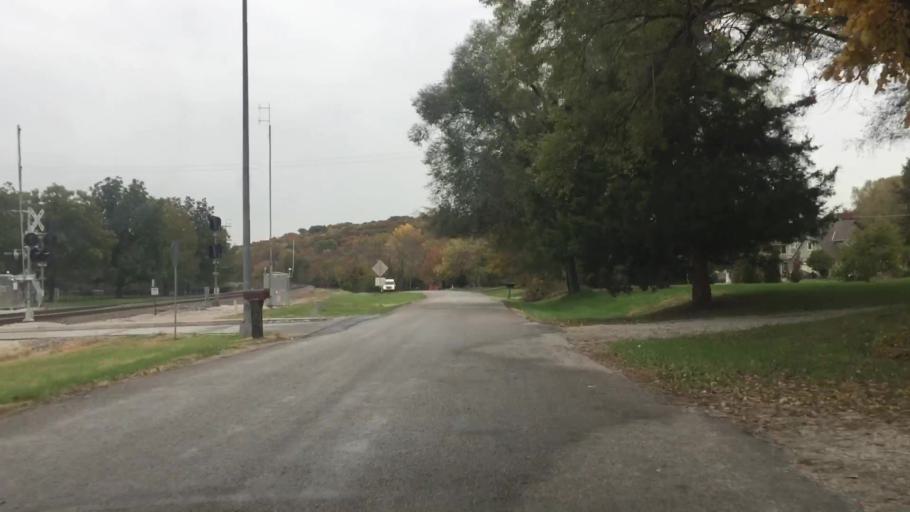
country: US
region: Kansas
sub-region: Wyandotte County
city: Edwardsville
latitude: 38.9962
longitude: -94.8224
